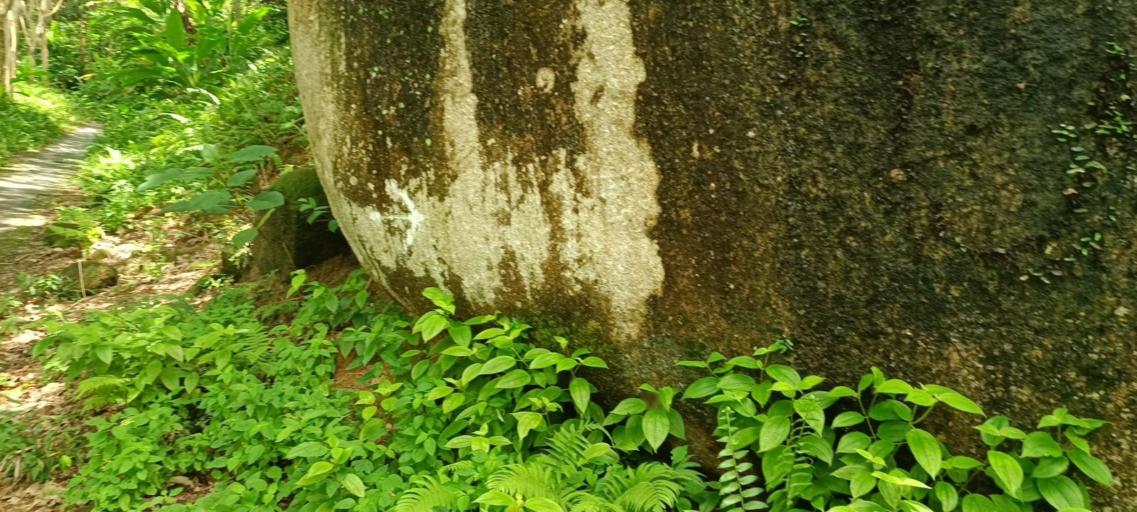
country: MY
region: Penang
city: Kampung Sungai Ara
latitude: 5.3013
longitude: 100.1912
